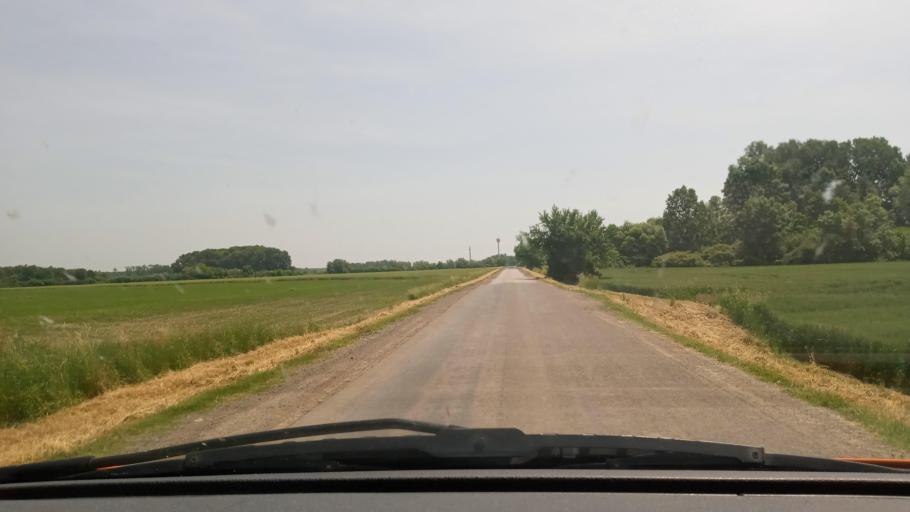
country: HU
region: Baranya
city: Szigetvar
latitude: 45.9833
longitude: 17.7347
